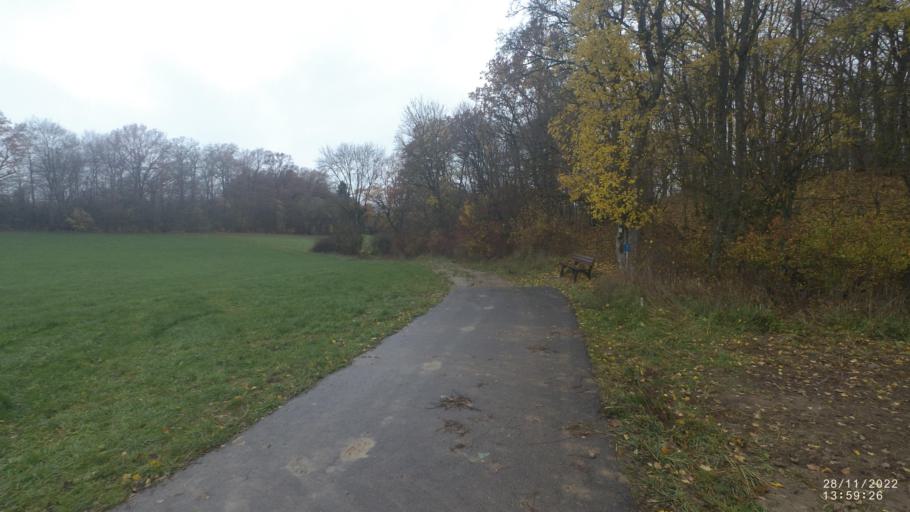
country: DE
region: Rheinland-Pfalz
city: Nohn
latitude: 50.3338
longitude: 6.7766
